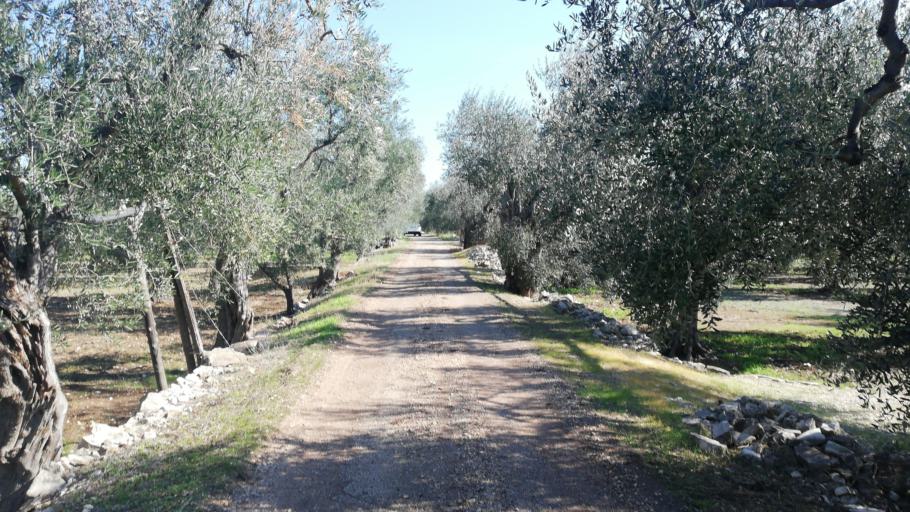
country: IT
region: Apulia
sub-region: Provincia di Bari
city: Bitonto
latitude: 41.1215
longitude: 16.6573
